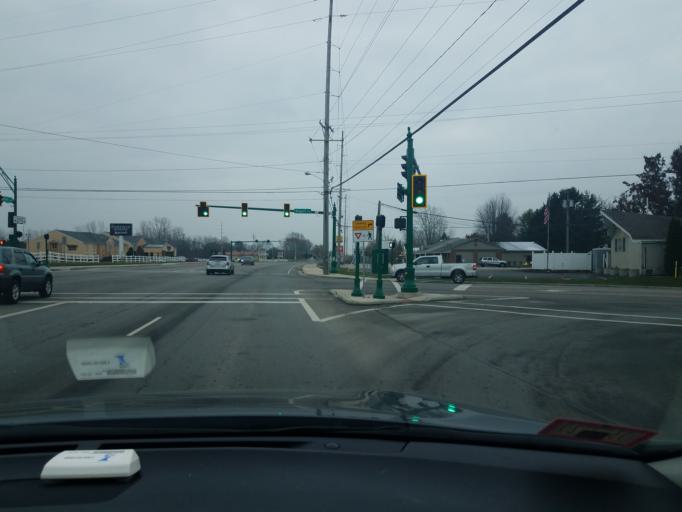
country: US
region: Ohio
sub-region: Erie County
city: Sandusky
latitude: 41.3960
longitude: -82.6519
